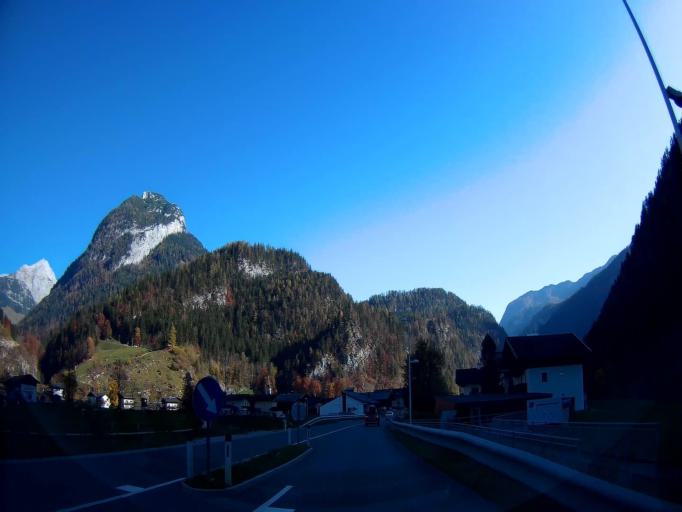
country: AT
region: Salzburg
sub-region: Politischer Bezirk Zell am See
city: Sankt Martin bei Lofer
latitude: 47.5218
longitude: 12.7502
